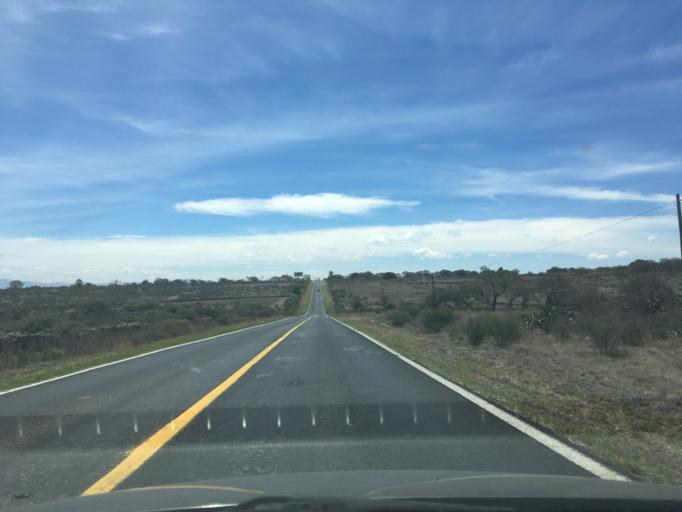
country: MX
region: Hidalgo
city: Huichapan
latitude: 20.4275
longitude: -99.5151
